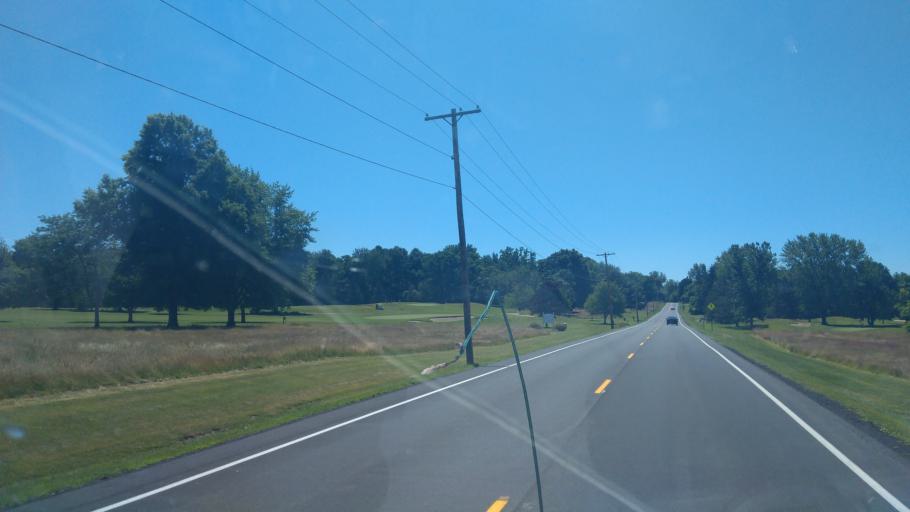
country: US
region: New York
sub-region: Wayne County
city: Sodus
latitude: 43.2485
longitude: -76.9908
